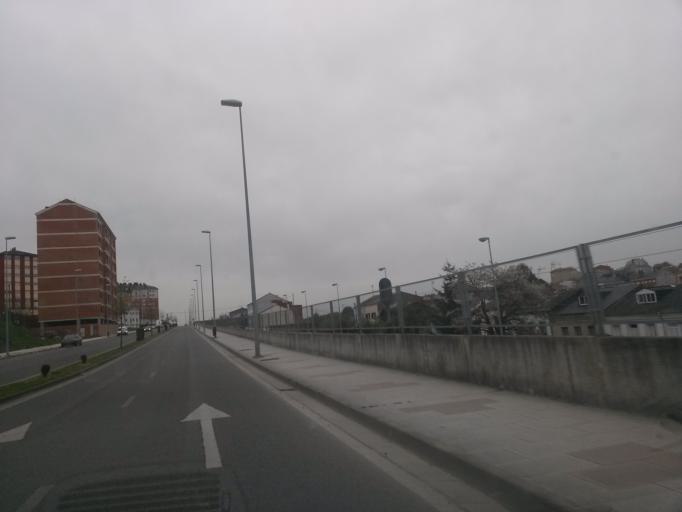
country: ES
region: Galicia
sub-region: Provincia de Lugo
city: Lugo
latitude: 43.0192
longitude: -7.5567
